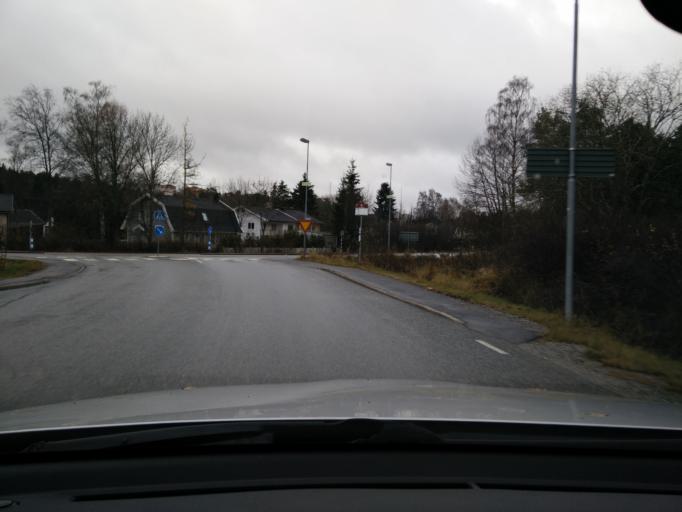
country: SE
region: Stockholm
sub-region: Sollentuna Kommun
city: Sollentuna
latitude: 59.4553
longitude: 17.9583
